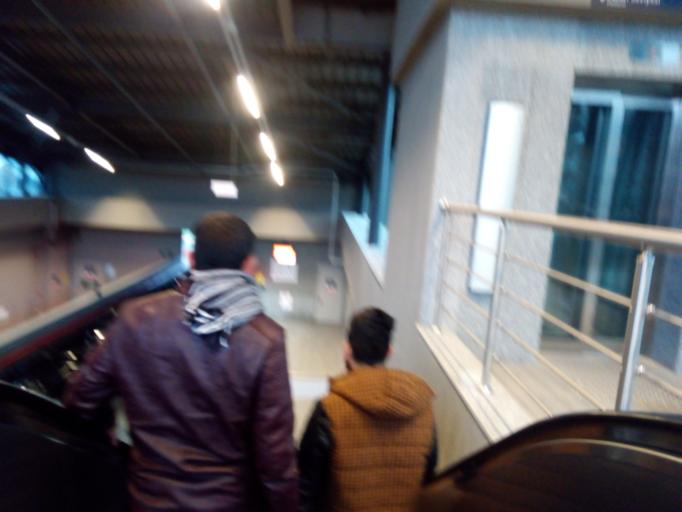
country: TR
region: Istanbul
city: Sisli
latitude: 41.1031
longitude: 28.9946
